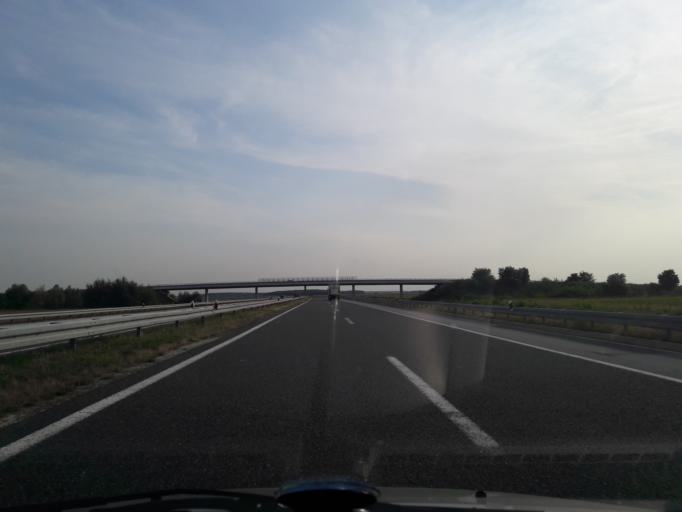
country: HR
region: Osjecko-Baranjska
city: Cepin
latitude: 45.5374
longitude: 18.5225
